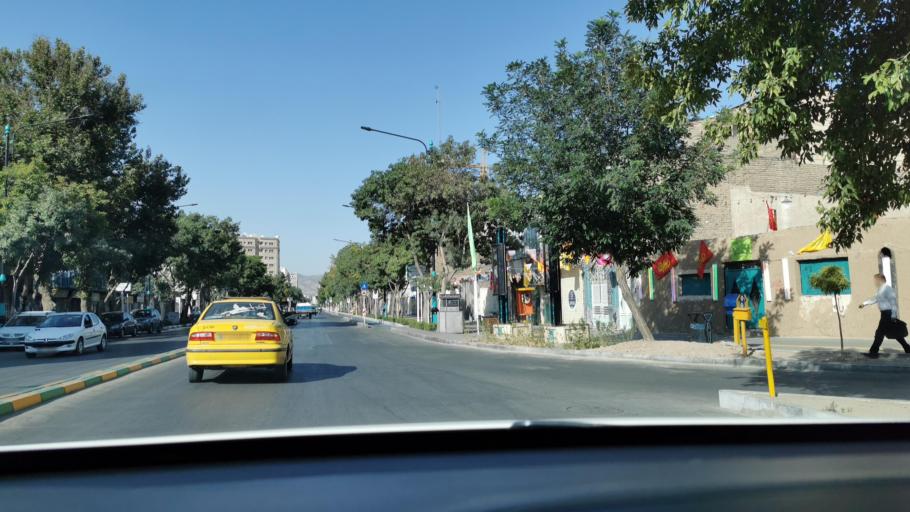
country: IR
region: Razavi Khorasan
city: Mashhad
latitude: 36.2996
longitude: 59.6177
